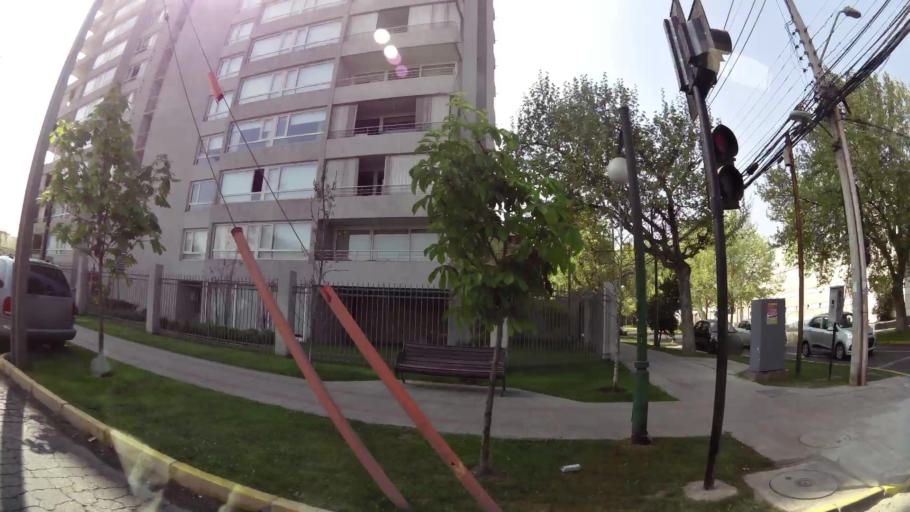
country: CL
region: Santiago Metropolitan
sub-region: Provincia de Santiago
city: Villa Presidente Frei, Nunoa, Santiago, Chile
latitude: -33.4479
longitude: -70.5987
